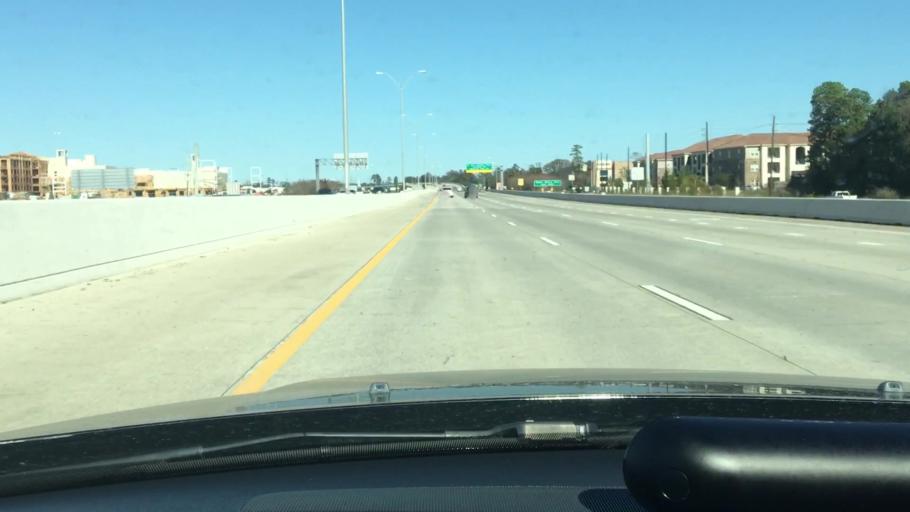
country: US
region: Texas
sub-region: Harris County
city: Atascocita
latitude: 29.9164
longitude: -95.2008
